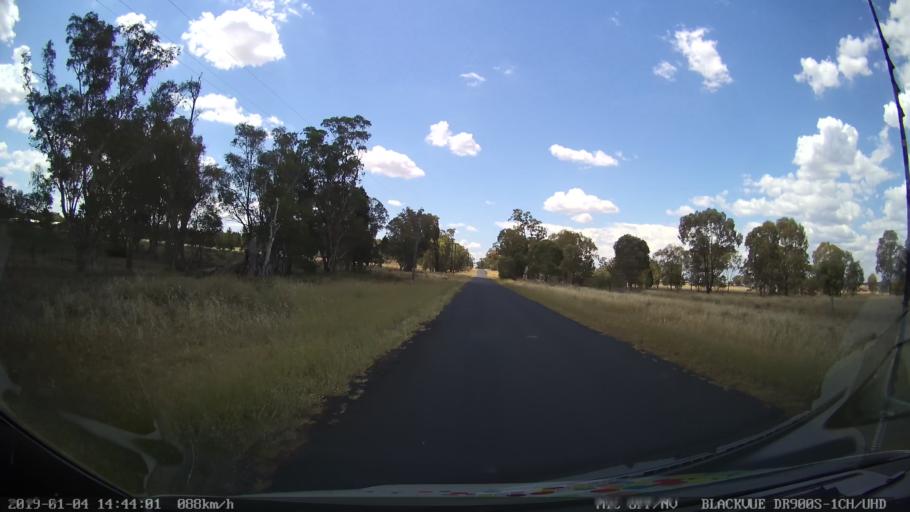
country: AU
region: New South Wales
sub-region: Dubbo Municipality
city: Dubbo
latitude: -32.1116
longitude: 148.6547
